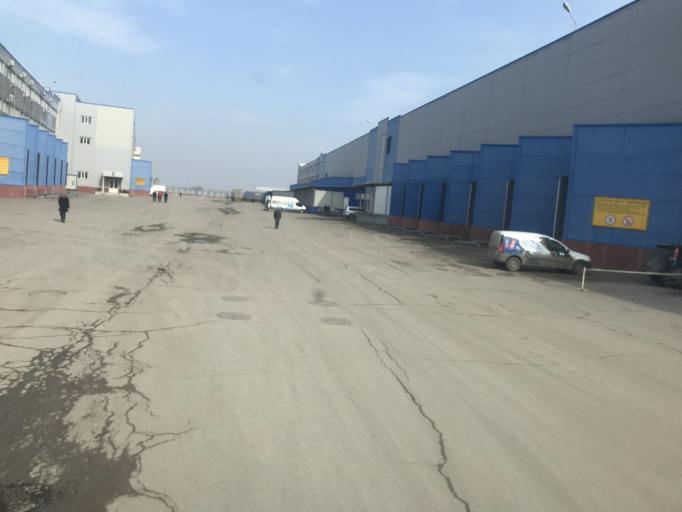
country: KZ
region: Almaty Oblysy
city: Pervomayskiy
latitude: 43.3619
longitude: 76.9762
